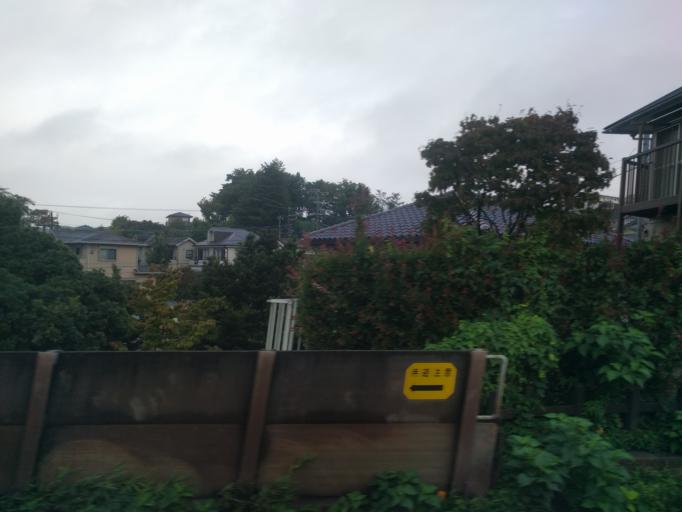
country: JP
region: Tokyo
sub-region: Machida-shi
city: Machida
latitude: 35.5382
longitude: 139.5070
